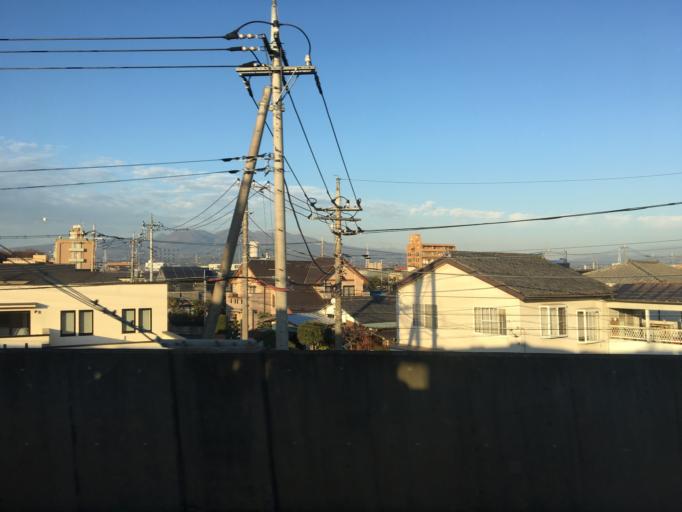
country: JP
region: Gunma
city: Maebashi-shi
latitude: 36.3800
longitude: 139.0937
